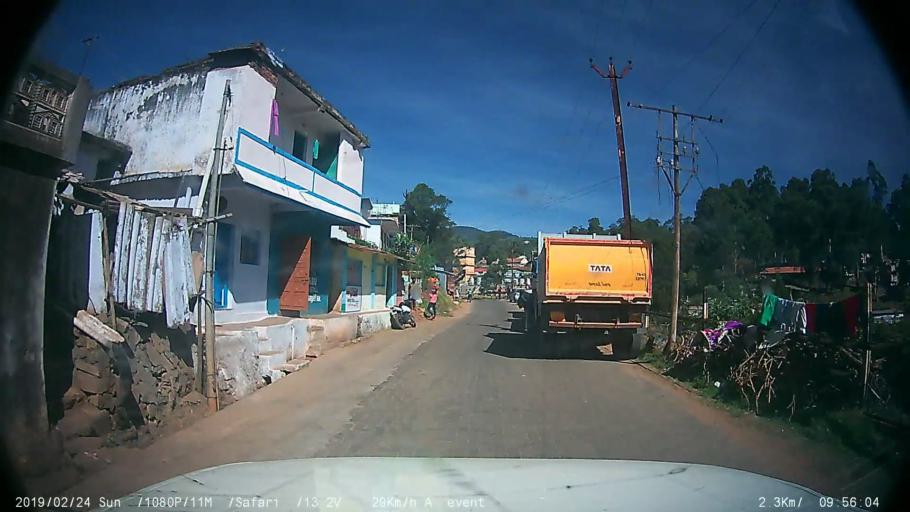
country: IN
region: Tamil Nadu
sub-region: Nilgiri
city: Wellington
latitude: 11.3587
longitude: 76.7719
